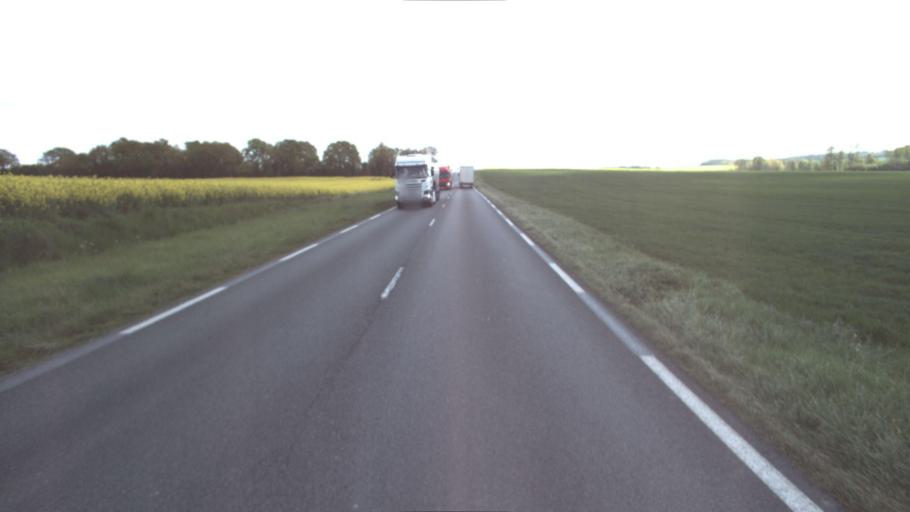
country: FR
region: Ile-de-France
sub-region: Departement de Seine-et-Marne
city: Choisy-en-Brie
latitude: 48.6981
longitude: 3.2752
